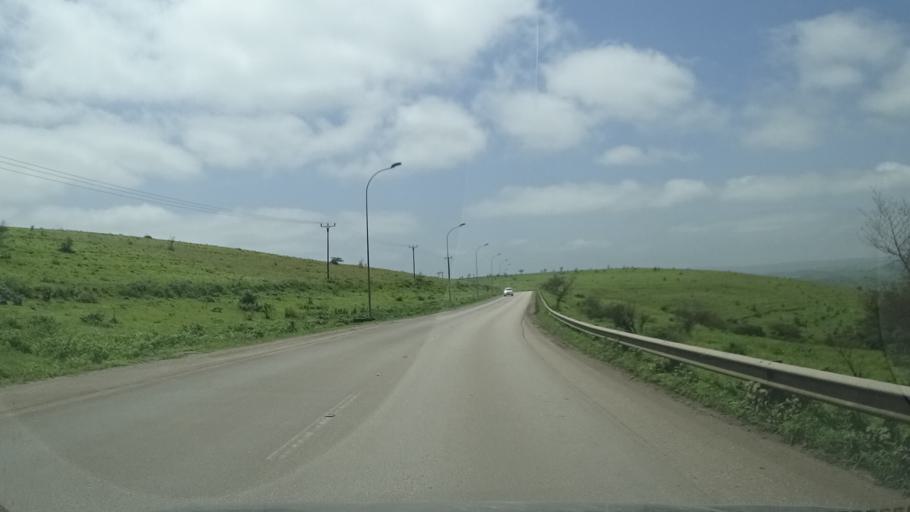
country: OM
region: Zufar
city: Salalah
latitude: 17.1710
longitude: 54.2341
